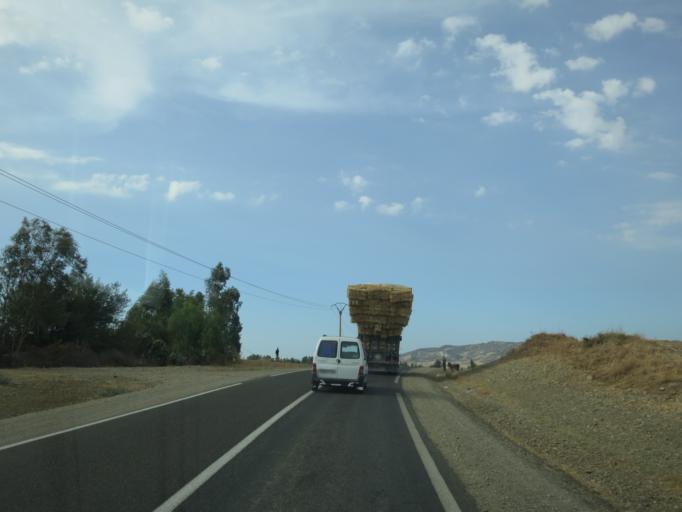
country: MA
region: Gharb-Chrarda-Beni Hssen
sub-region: Sidi-Kacem
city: Sidi Bousber
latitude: 34.5150
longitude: -5.5066
